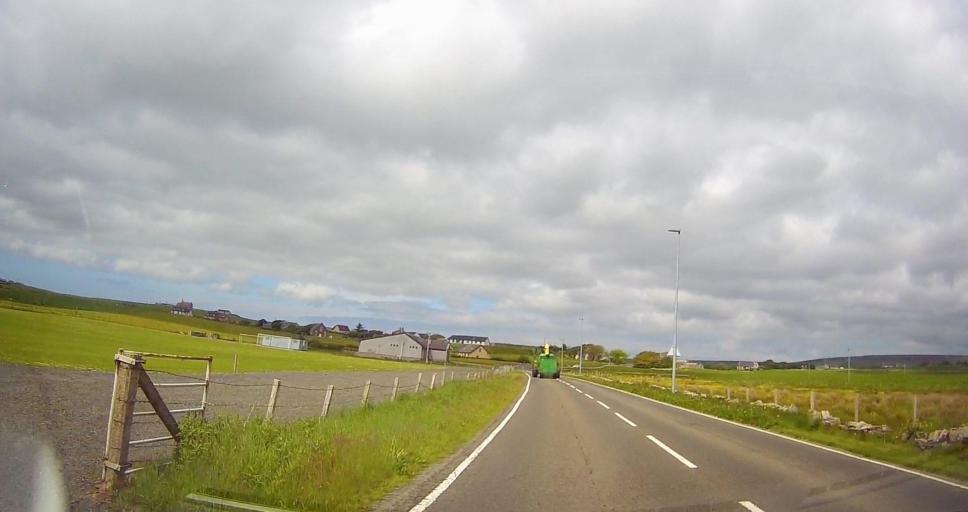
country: GB
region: Scotland
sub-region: Orkney Islands
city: Stromness
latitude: 59.0371
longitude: -3.1867
